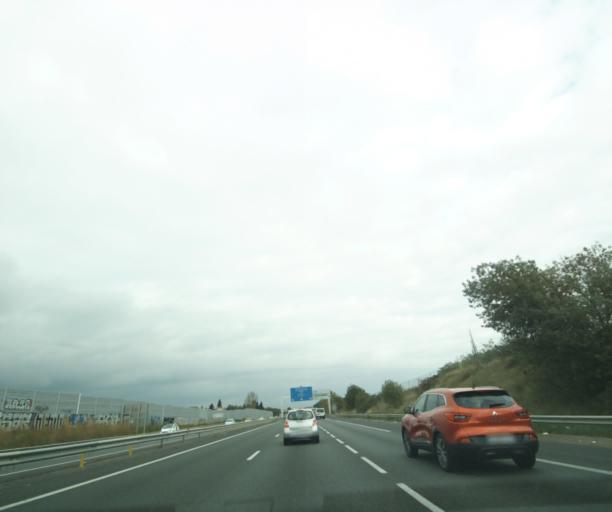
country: FR
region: Languedoc-Roussillon
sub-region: Departement de l'Herault
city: Lattes
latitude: 43.5834
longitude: 3.8886
